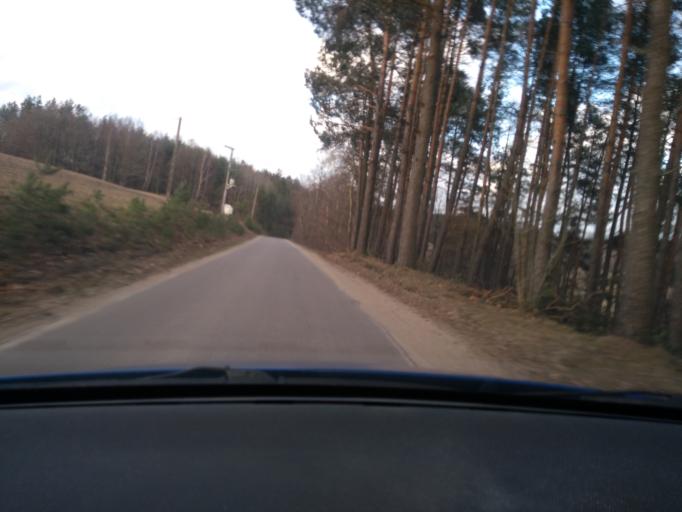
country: PL
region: Pomeranian Voivodeship
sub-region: Powiat kartuski
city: Przodkowo
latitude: 54.4132
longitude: 18.2376
